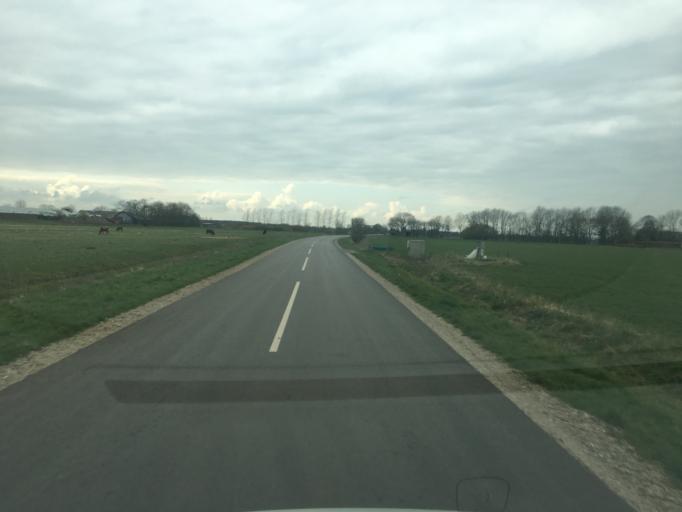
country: DK
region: South Denmark
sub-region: Tonder Kommune
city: Logumkloster
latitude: 55.0611
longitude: 9.0538
